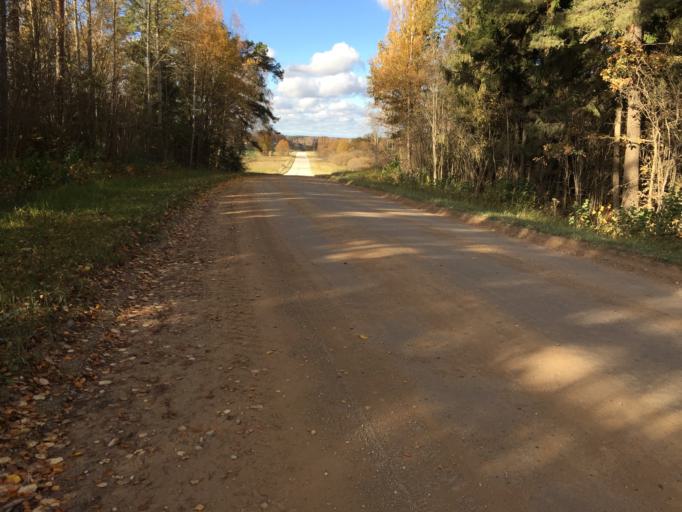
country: LV
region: Tukuma Rajons
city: Tukums
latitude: 56.9629
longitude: 22.9738
